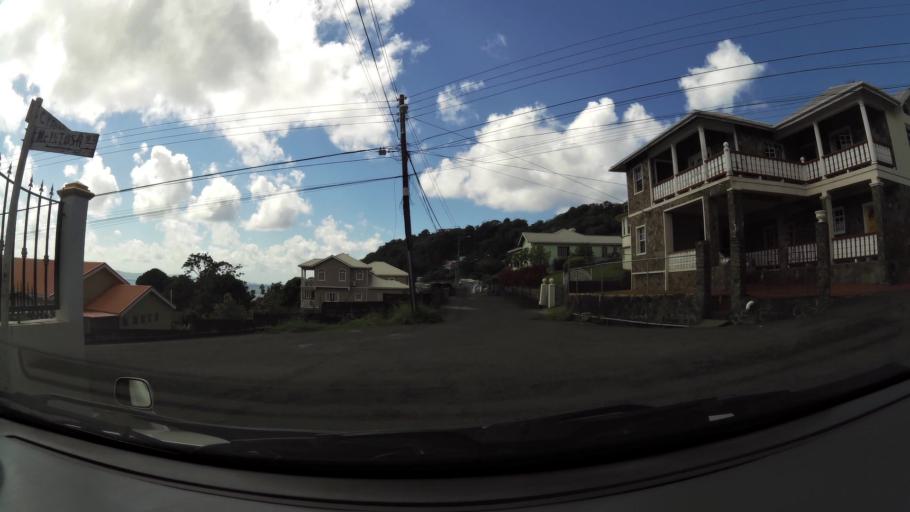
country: VC
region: Saint George
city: Kingstown Park
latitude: 13.1617
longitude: -61.2303
